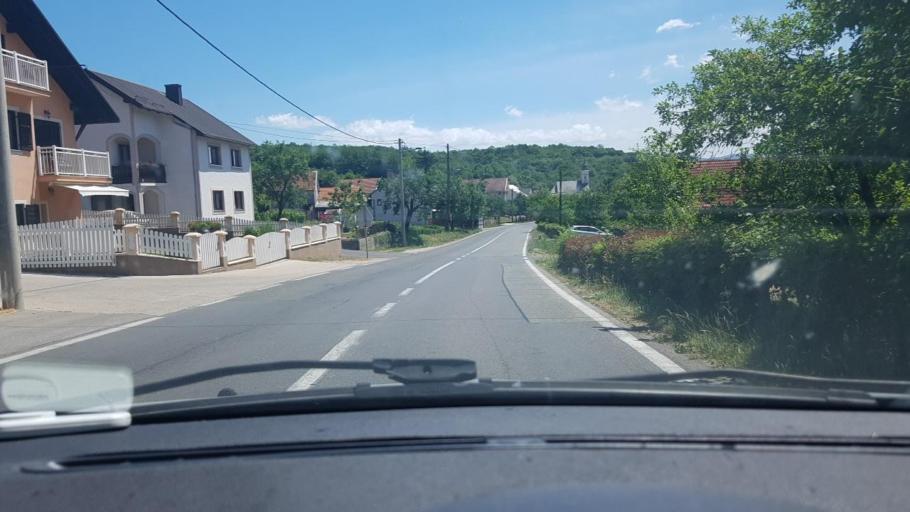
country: HR
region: Licko-Senjska
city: Otocac
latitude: 44.8733
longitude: 15.2150
